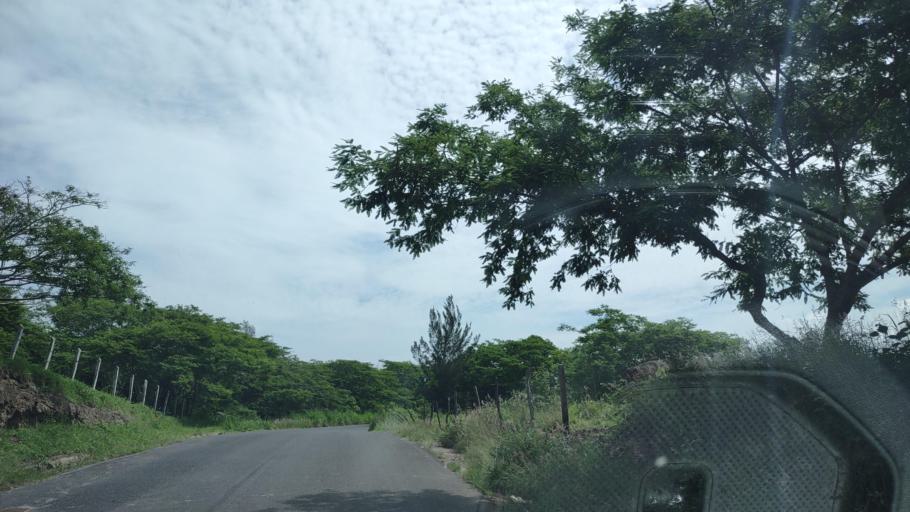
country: MX
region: Veracruz
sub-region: Emiliano Zapata
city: Dos Rios
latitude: 19.4718
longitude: -96.8289
